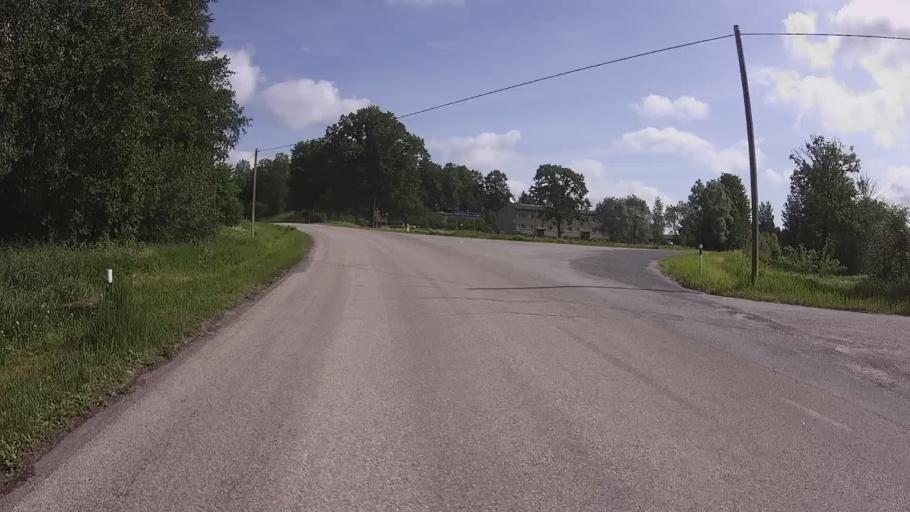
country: EE
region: Vorumaa
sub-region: Antsla vald
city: Vana-Antsla
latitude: 57.8613
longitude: 26.6082
